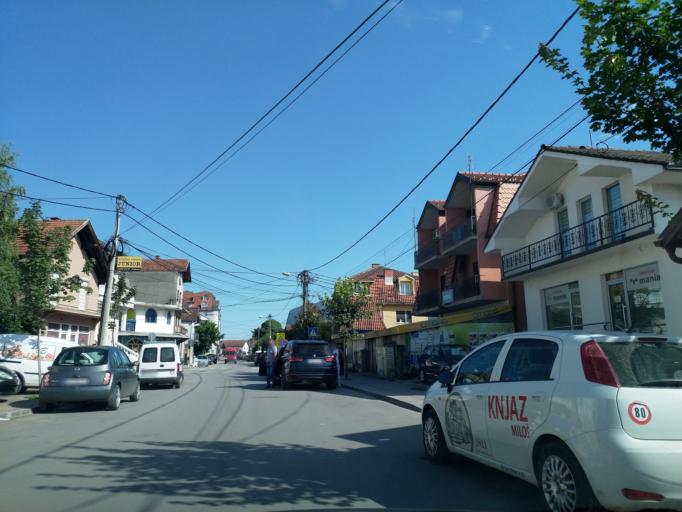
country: RS
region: Central Serbia
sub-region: Pomoravski Okrug
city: Paracin
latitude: 43.8569
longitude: 21.4108
